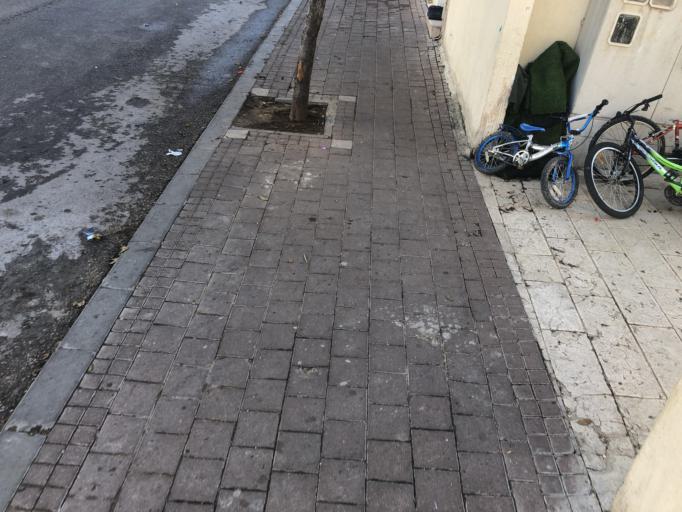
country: IL
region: Jerusalem
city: Modiin Ilit
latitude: 31.9230
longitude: 35.0469
